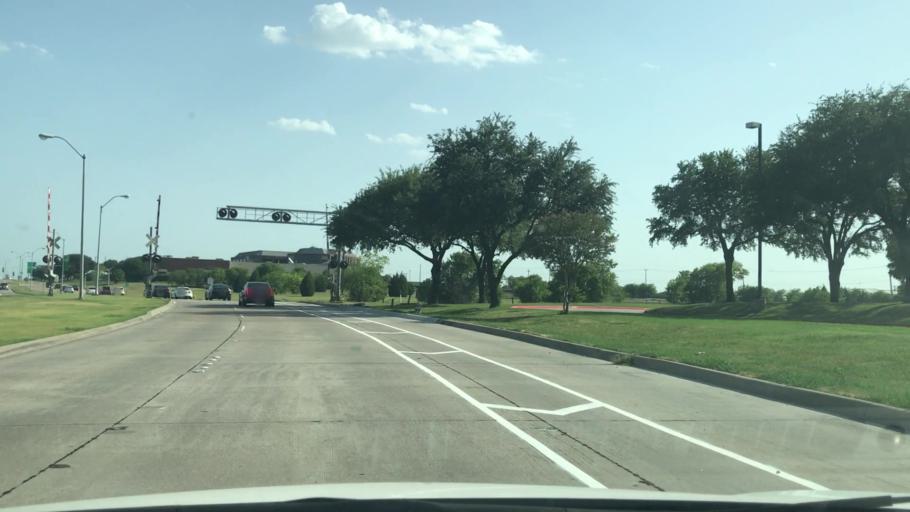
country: US
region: Texas
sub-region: Dallas County
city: Richardson
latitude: 32.9957
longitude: -96.7563
